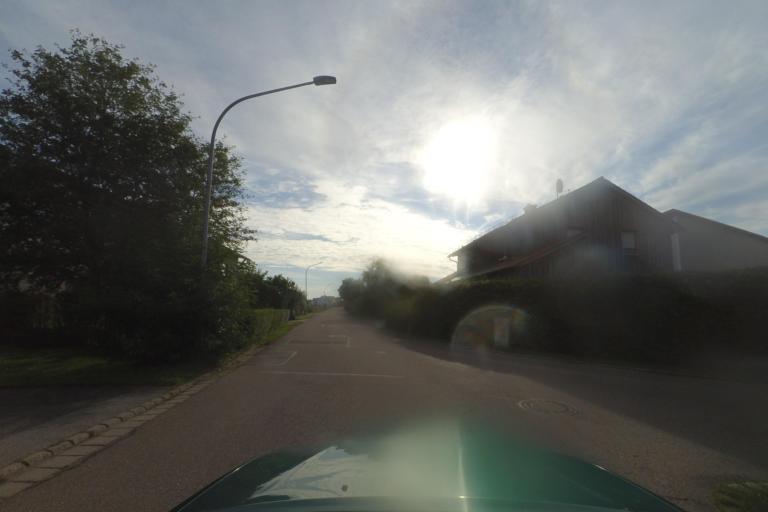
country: DE
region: Bavaria
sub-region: Upper Bavaria
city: Denkendorf
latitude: 48.9815
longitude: 11.4920
